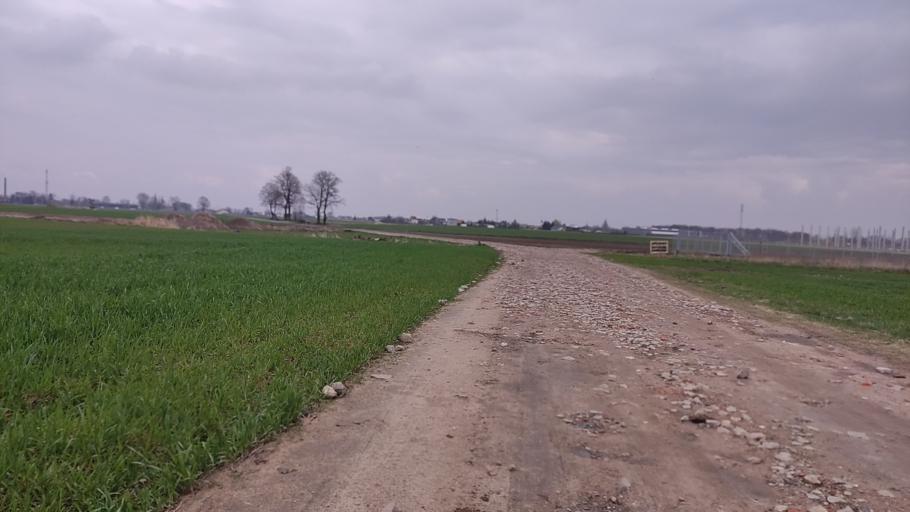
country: PL
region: Greater Poland Voivodeship
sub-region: Powiat poznanski
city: Swarzedz
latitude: 52.4043
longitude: 17.1432
